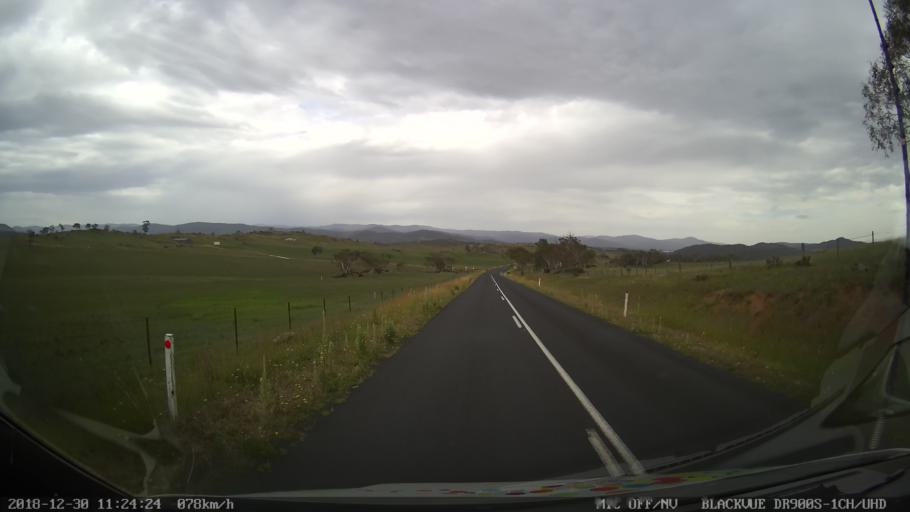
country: AU
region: New South Wales
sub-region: Snowy River
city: Jindabyne
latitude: -36.4837
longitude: 148.6506
